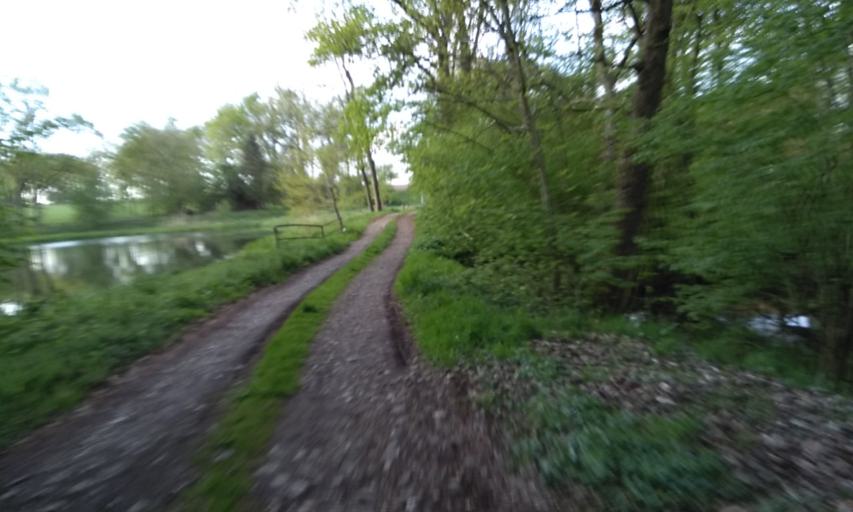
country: DE
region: Lower Saxony
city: Regesbostel
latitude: 53.4076
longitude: 9.6428
